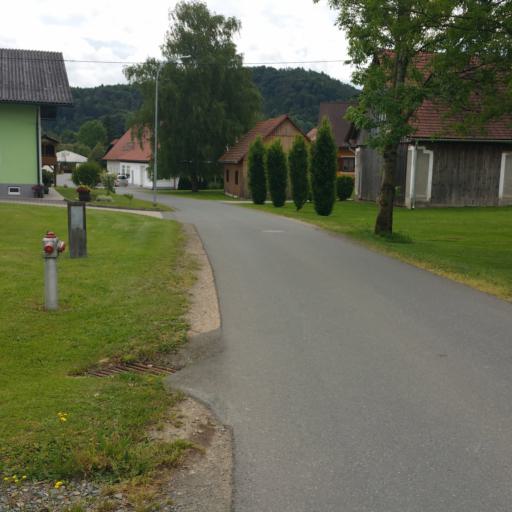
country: AT
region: Styria
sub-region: Politischer Bezirk Leibnitz
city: Gleinstatten
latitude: 46.7439
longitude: 15.3428
